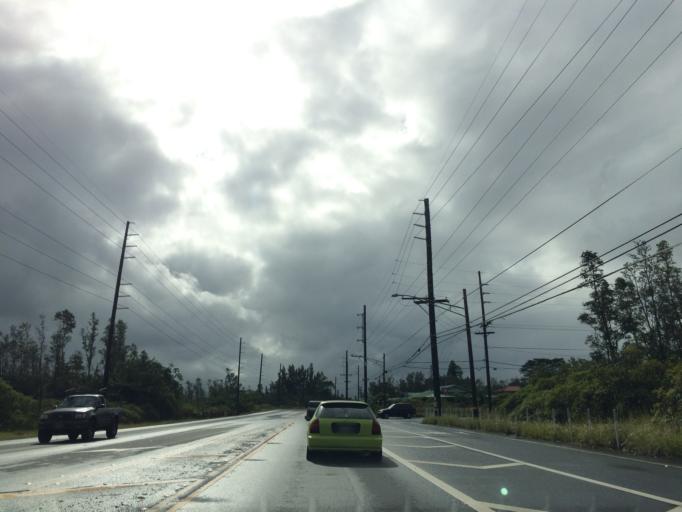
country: US
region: Hawaii
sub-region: Hawaii County
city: Ainaloa
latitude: 19.5440
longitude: -154.9754
